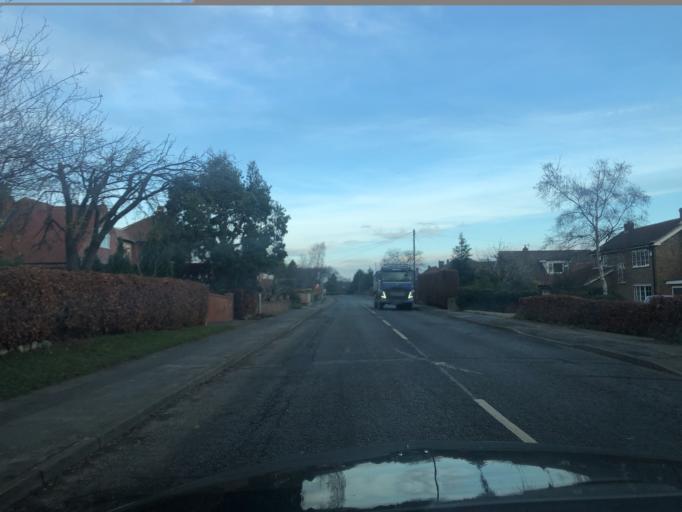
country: GB
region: England
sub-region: North Yorkshire
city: Bedale
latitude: 54.2844
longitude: -1.5984
